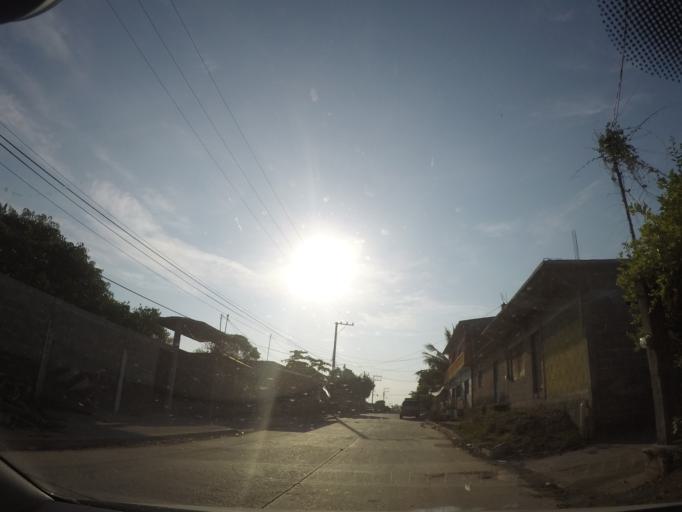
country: MX
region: Oaxaca
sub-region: Santo Domingo Tehuantepec
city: La Noria
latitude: 16.2466
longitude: -95.1467
